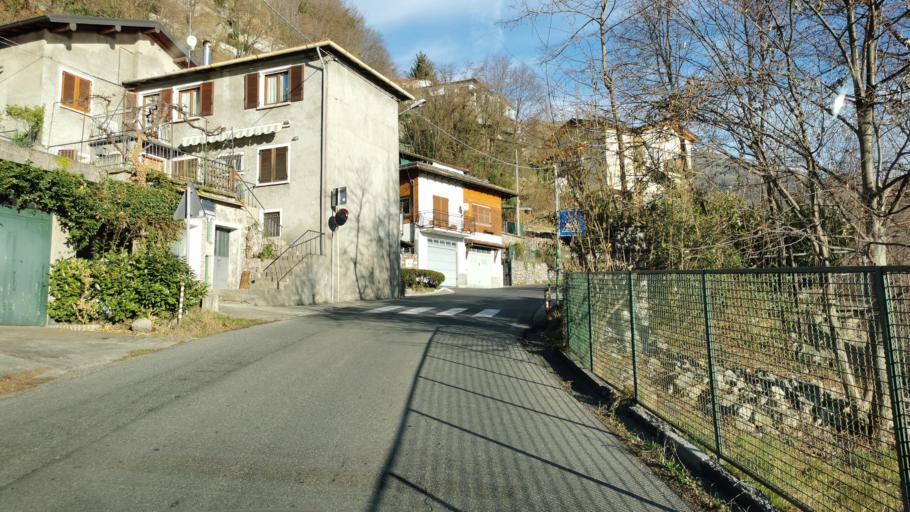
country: IT
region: Lombardy
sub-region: Provincia di Como
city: Menaggio
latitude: 46.0324
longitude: 9.2316
